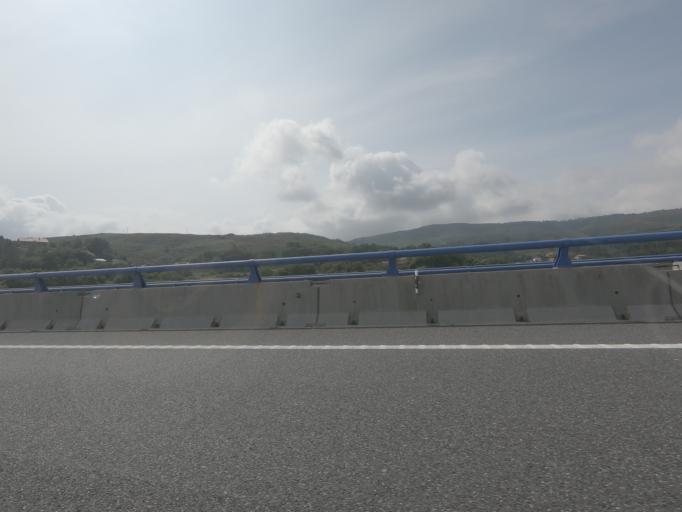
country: ES
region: Galicia
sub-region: Provincia de Pontevedra
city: Covelo
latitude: 42.1952
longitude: -8.3069
